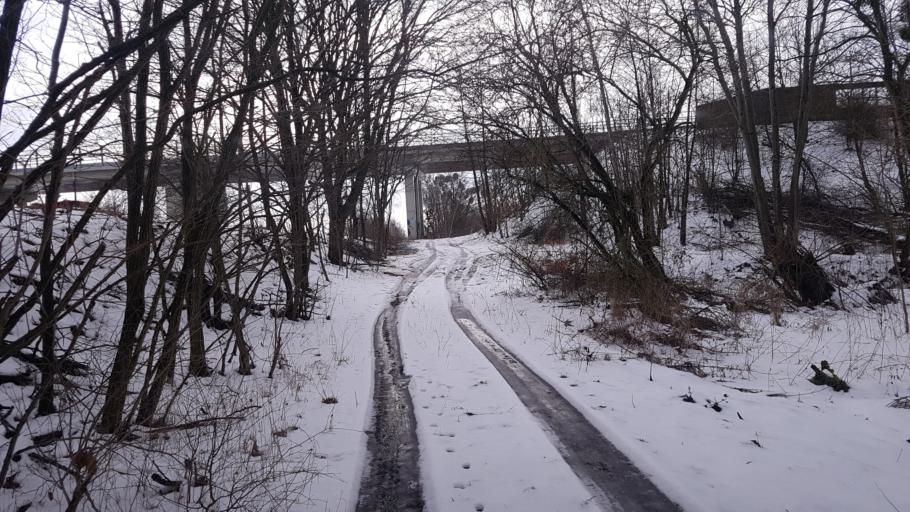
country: DE
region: Brandenburg
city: Grossraschen
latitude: 51.5839
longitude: 14.0162
